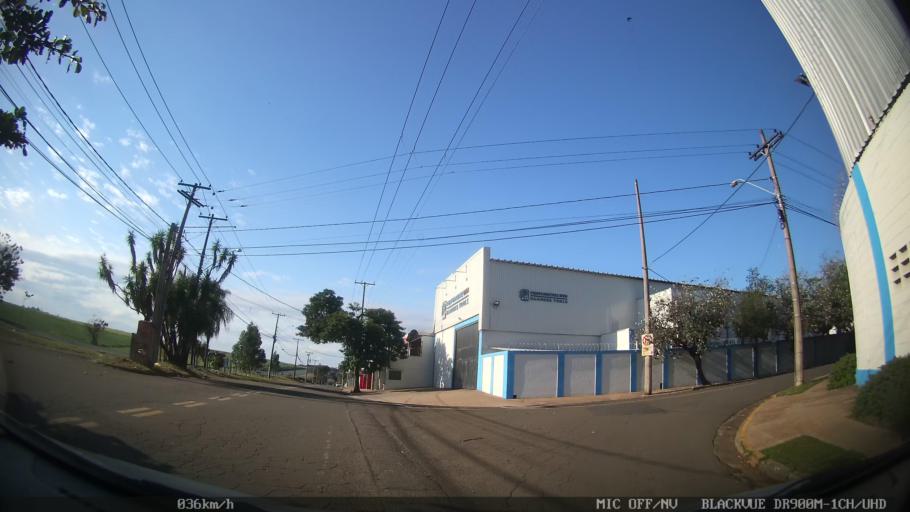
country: BR
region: Sao Paulo
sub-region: Piracicaba
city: Piracicaba
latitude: -22.6832
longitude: -47.6369
